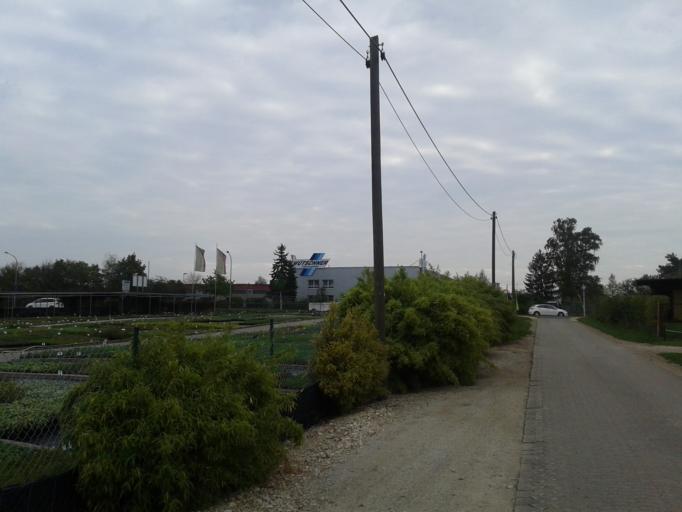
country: DE
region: Bavaria
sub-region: Upper Franconia
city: Bamberg
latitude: 49.9146
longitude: 10.8959
